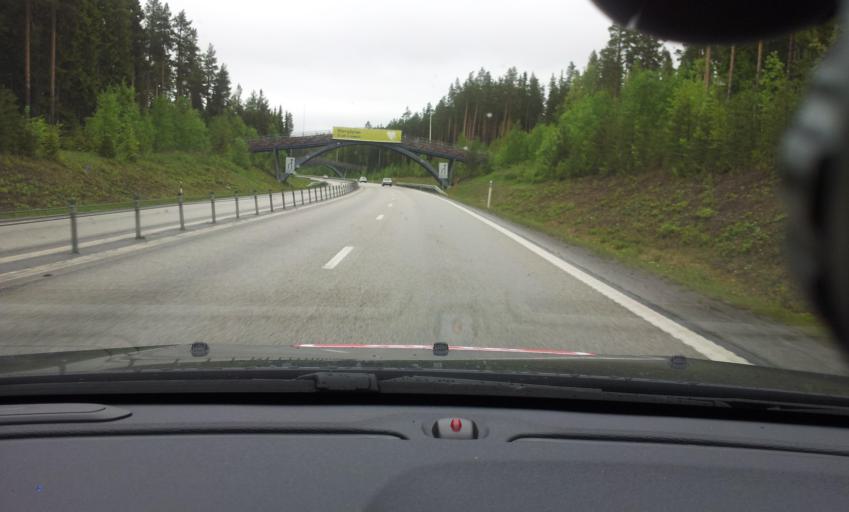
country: SE
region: Jaemtland
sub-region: OEstersunds Kommun
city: Ostersund
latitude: 63.1901
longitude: 14.6902
